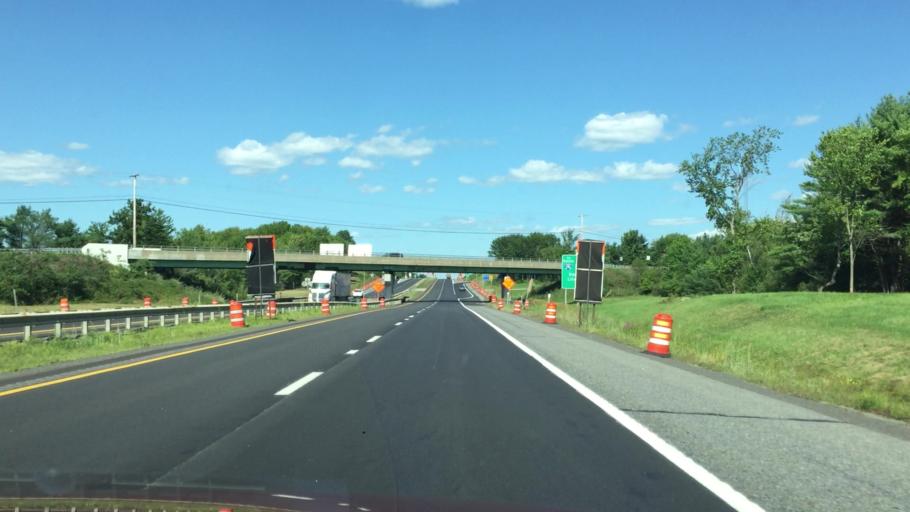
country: US
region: Maine
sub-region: Kennebec County
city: Gardiner
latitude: 44.2075
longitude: -69.8336
